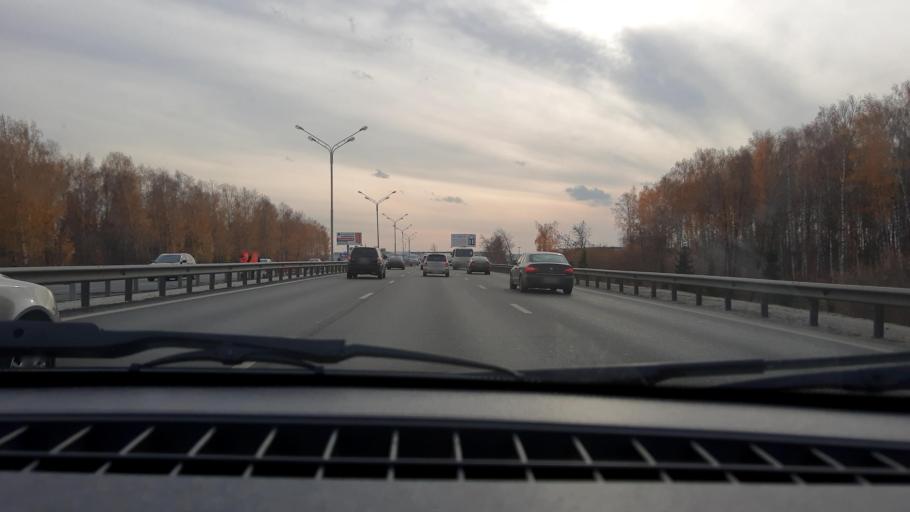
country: RU
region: Bashkortostan
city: Ufa
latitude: 54.6841
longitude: 55.9371
